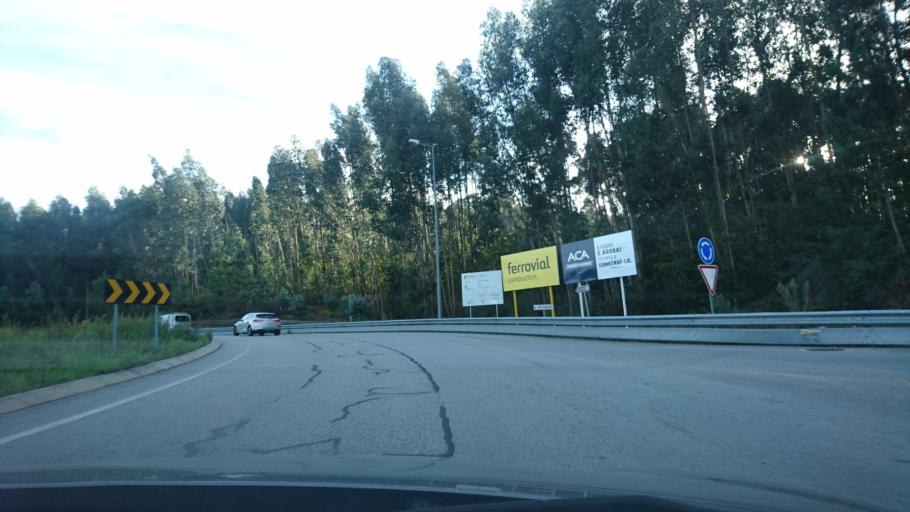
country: PT
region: Aveiro
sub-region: Santa Maria da Feira
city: Milheiros de Poiares
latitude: 40.9378
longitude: -8.4746
